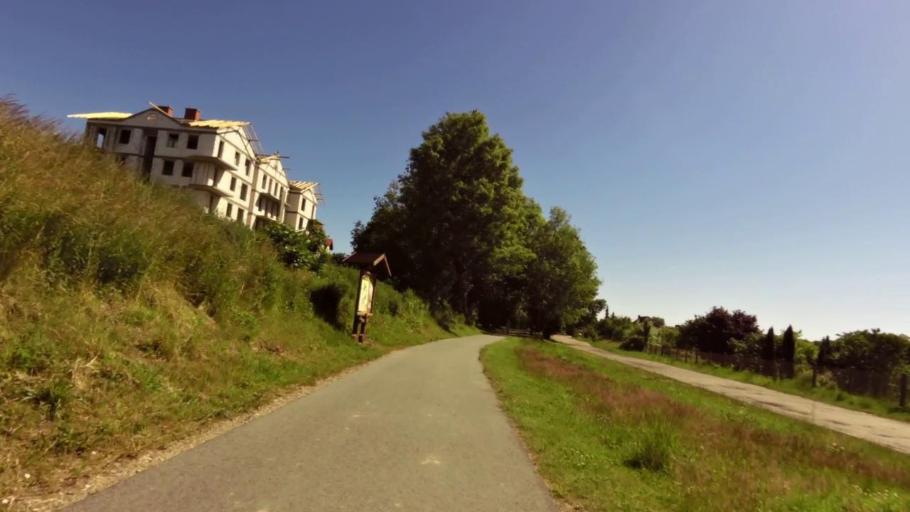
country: PL
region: West Pomeranian Voivodeship
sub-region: Powiat bialogardzki
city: Karlino
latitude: 54.0429
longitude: 15.8805
